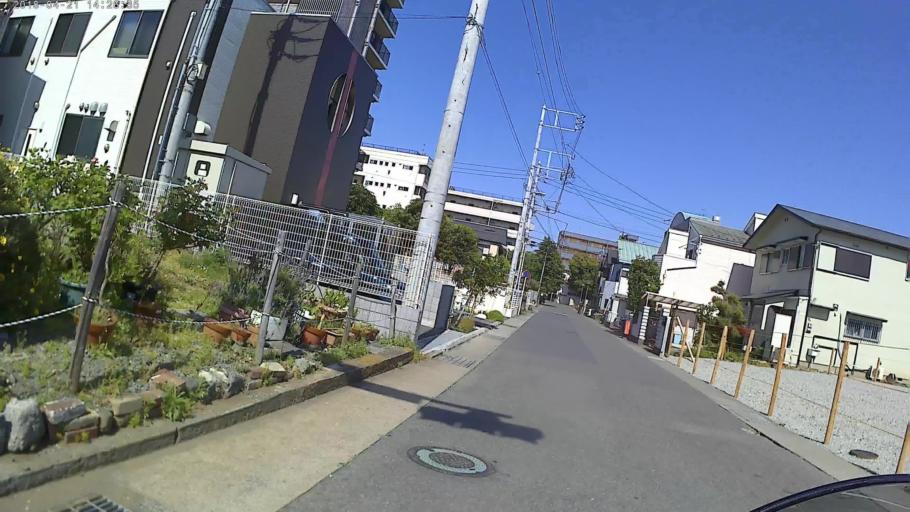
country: JP
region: Kanagawa
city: Hiratsuka
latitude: 35.3356
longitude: 139.3384
